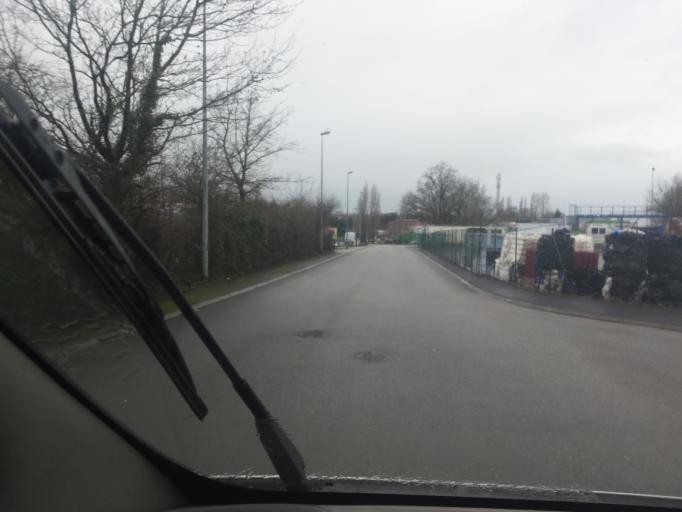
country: FR
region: Pays de la Loire
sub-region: Departement de la Vendee
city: La Roche-sur-Yon
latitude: 46.6405
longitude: -1.4112
